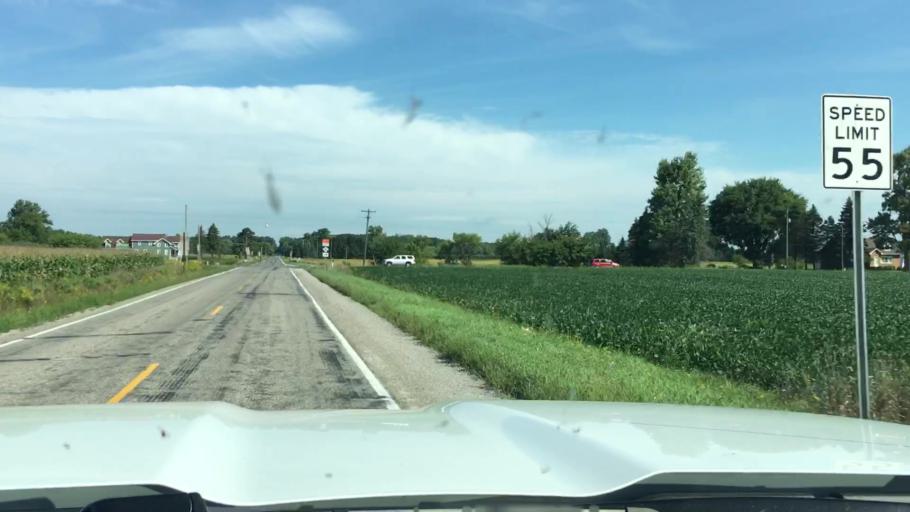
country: US
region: Michigan
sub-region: Saginaw County
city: Hemlock
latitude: 43.4495
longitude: -84.2302
